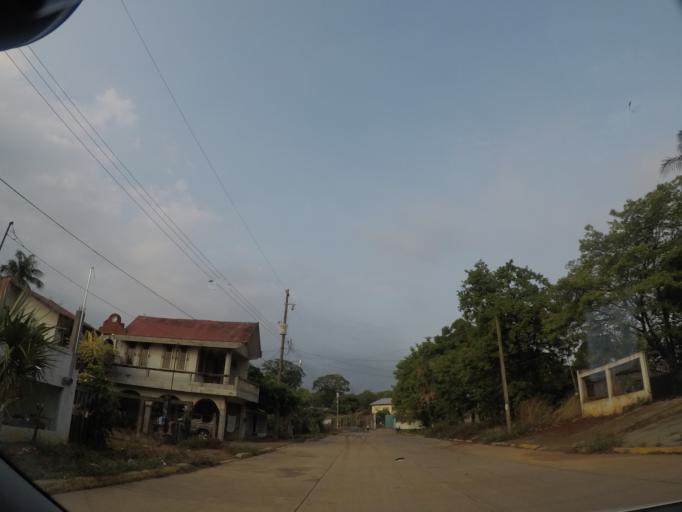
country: MX
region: Oaxaca
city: Matias Romero
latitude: 16.8713
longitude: -95.0399
